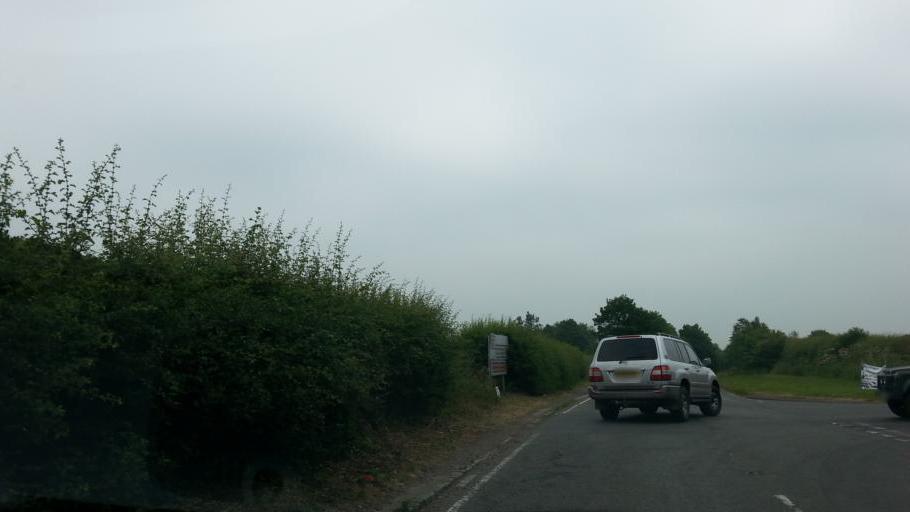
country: GB
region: England
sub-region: Staffordshire
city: Rugeley
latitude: 52.8252
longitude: -1.8953
